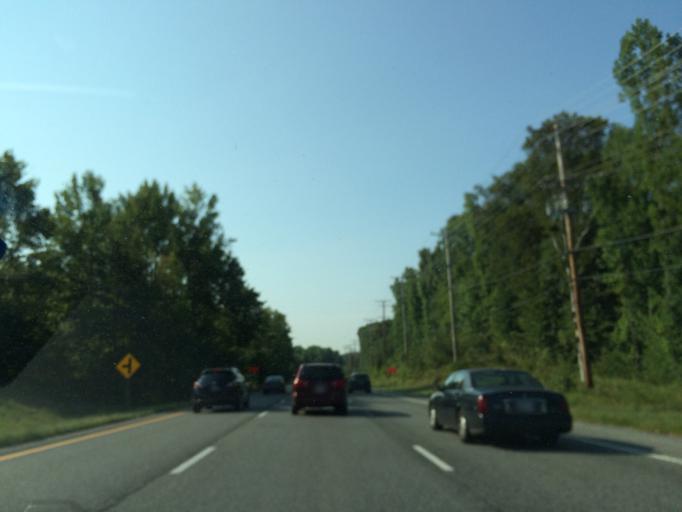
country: US
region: Maryland
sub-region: Prince George's County
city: Bowie
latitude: 38.9325
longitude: -76.7176
